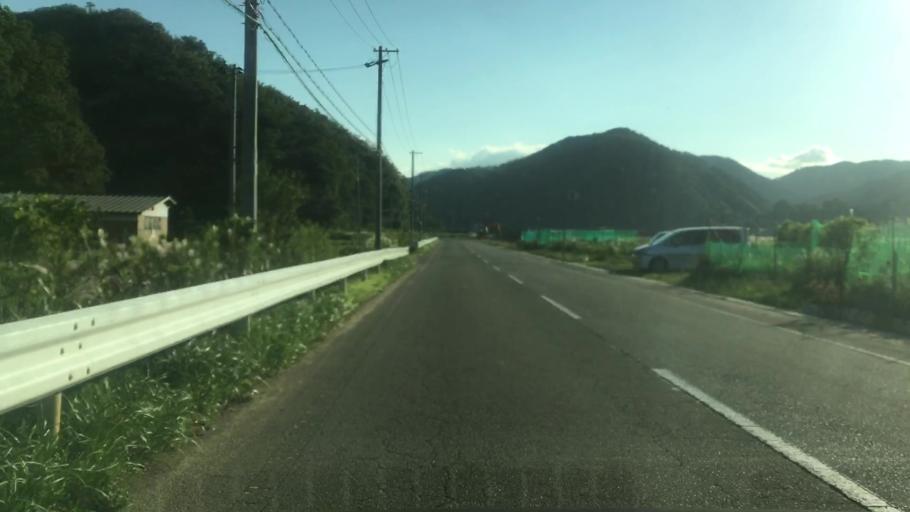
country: JP
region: Hyogo
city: Toyooka
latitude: 35.6119
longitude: 134.8100
